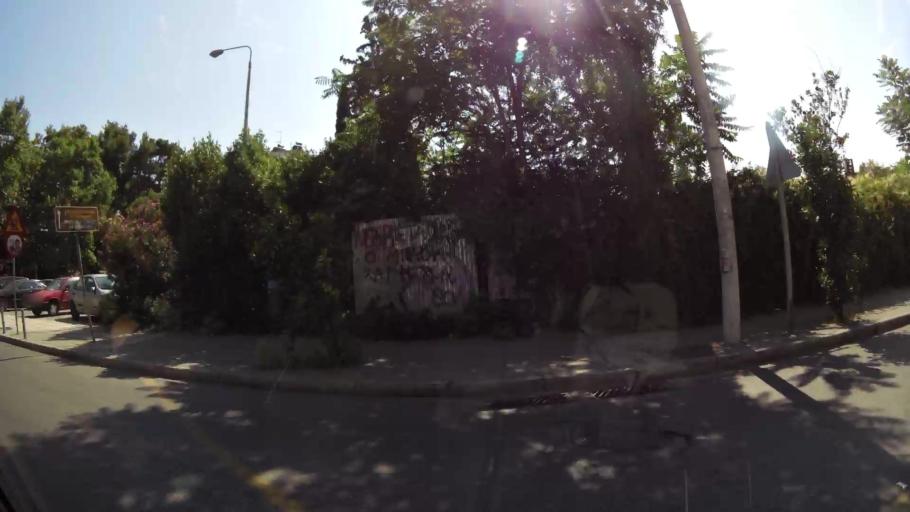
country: GR
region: Central Macedonia
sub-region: Nomos Thessalonikis
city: Kalamaria
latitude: 40.5956
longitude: 22.9535
